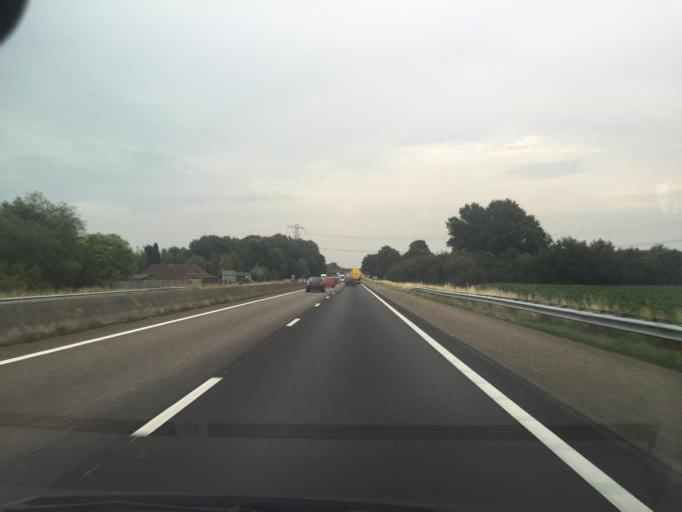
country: NL
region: Limburg
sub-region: Gemeente Peel en Maas
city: Maasbree
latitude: 51.3774
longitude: 5.9287
